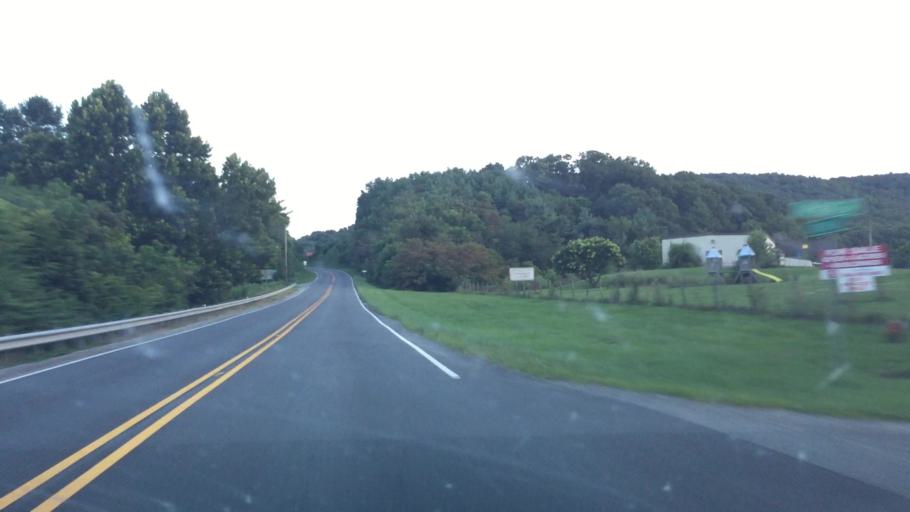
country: US
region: Virginia
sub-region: Wythe County
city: Wytheville
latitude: 36.9374
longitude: -80.9442
